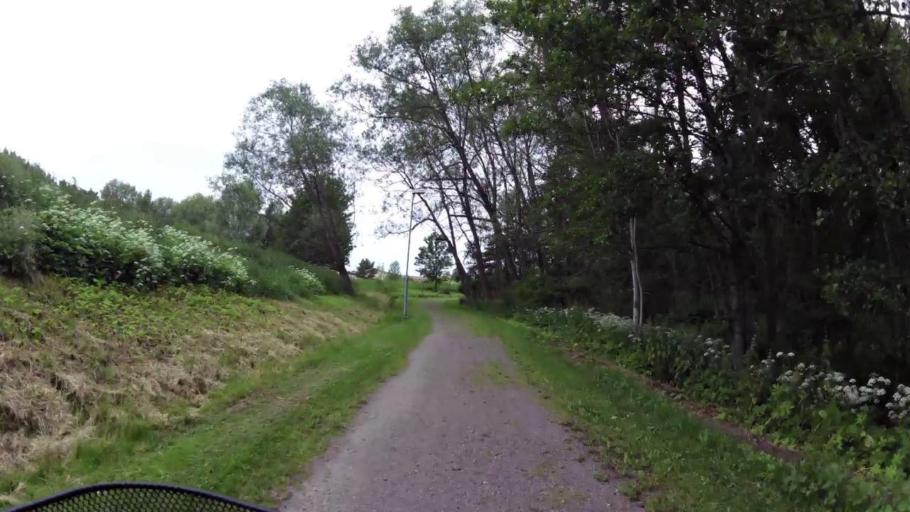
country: SE
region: OEstergoetland
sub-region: Linkopings Kommun
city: Linkoping
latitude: 58.3709
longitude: 15.6633
